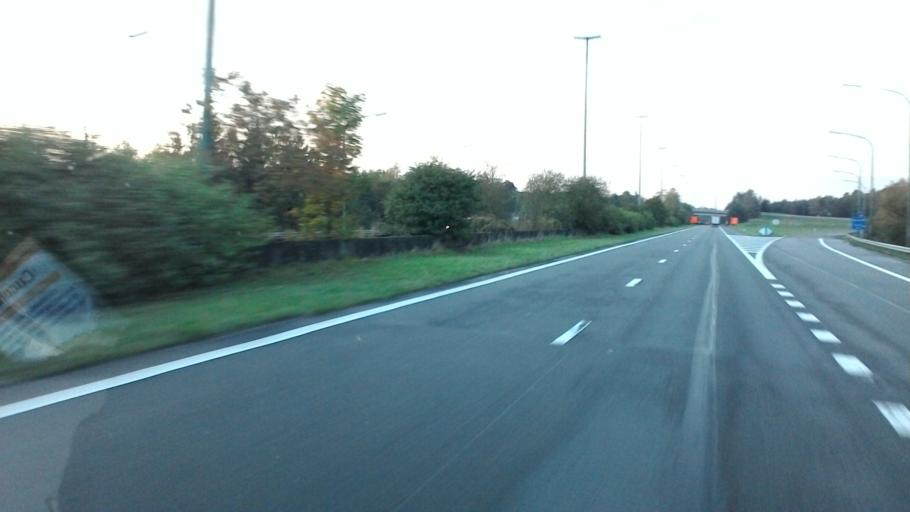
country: BE
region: Wallonia
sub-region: Province de Liege
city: Aywaille
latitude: 50.4226
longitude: 5.7040
